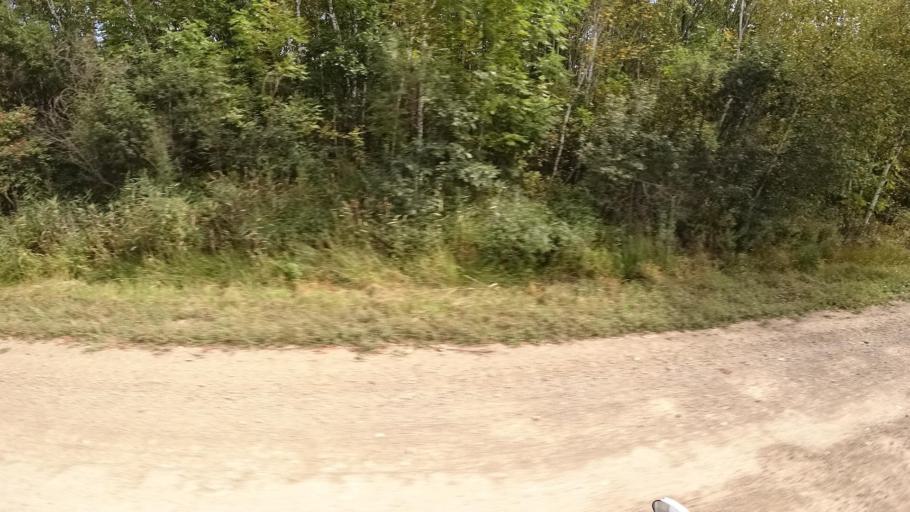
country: RU
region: Primorskiy
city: Yakovlevka
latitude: 44.7428
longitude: 133.6066
